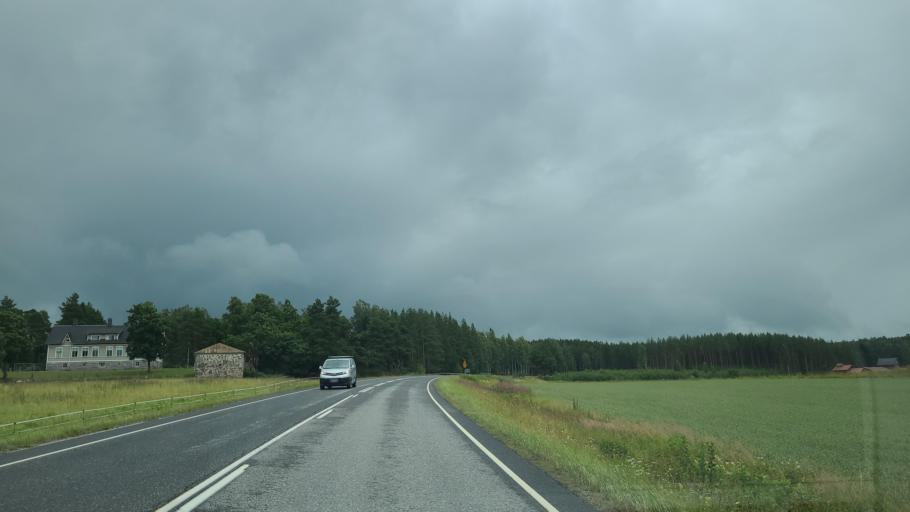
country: FI
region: Varsinais-Suomi
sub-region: Turku
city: Sauvo
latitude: 60.3299
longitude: 22.7134
